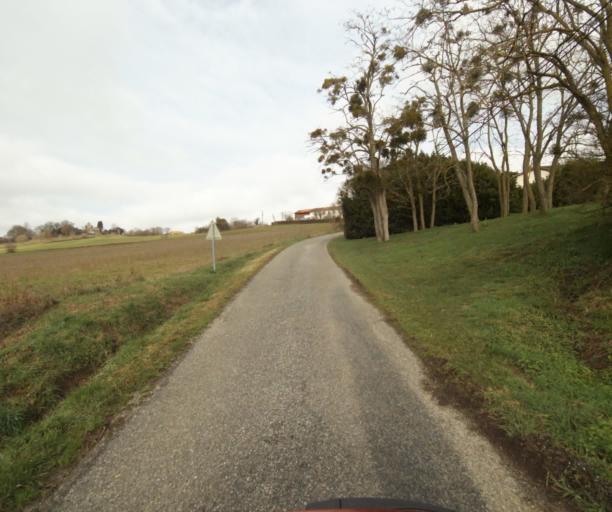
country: FR
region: Midi-Pyrenees
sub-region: Departement de l'Ariege
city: Pamiers
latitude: 43.1028
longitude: 1.5223
